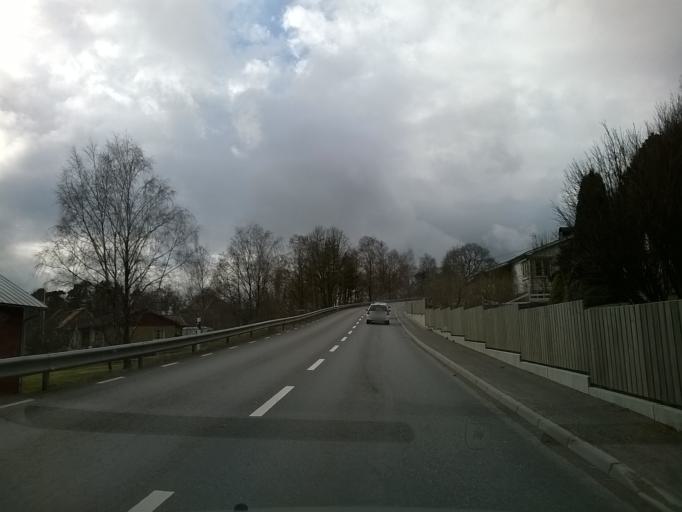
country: SE
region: Halland
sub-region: Varbergs Kommun
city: Tvaaker
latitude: 57.1431
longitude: 12.4654
